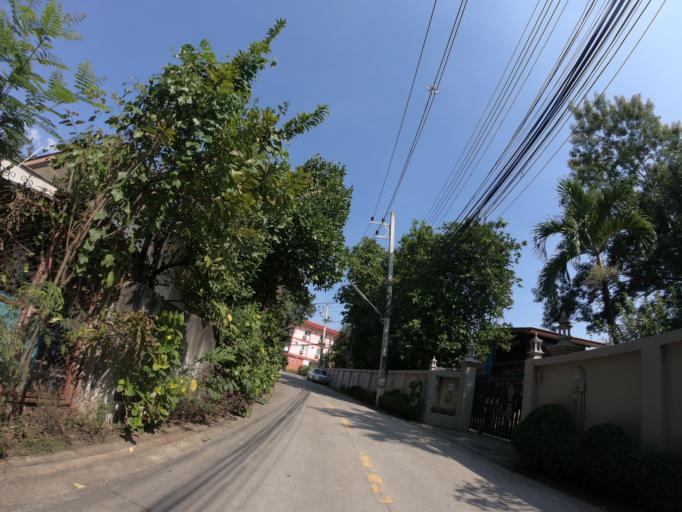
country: TH
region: Chiang Mai
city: Chiang Mai
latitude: 18.7768
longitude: 99.0223
